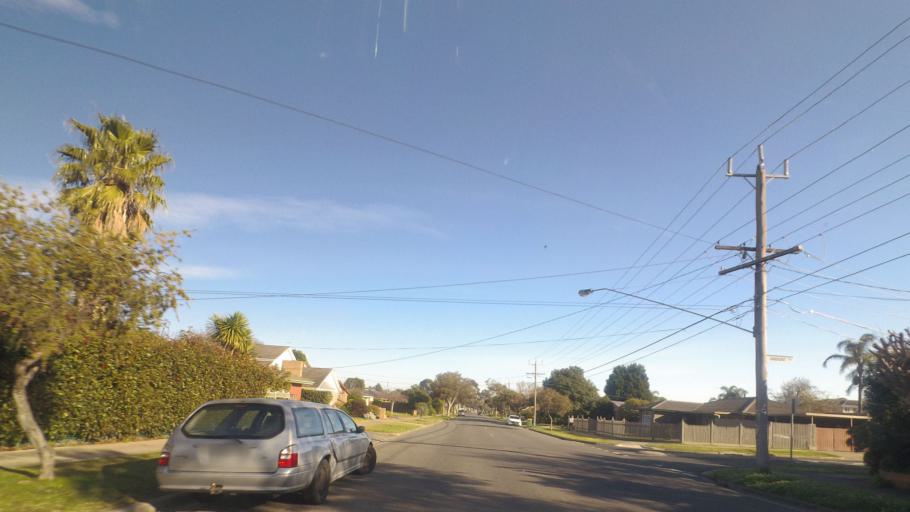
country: AU
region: Victoria
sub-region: Banyule
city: Bundoora
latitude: -37.6984
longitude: 145.0690
